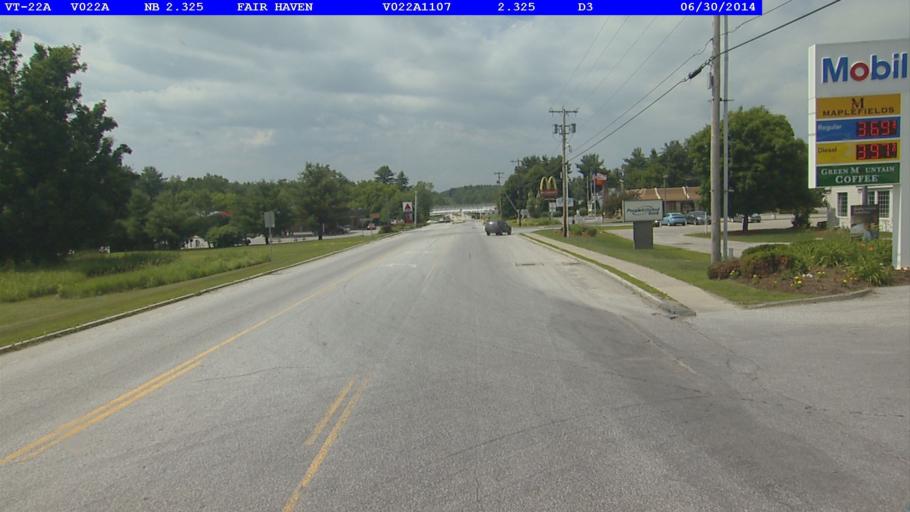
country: US
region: Vermont
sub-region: Rutland County
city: Fair Haven
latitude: 43.6032
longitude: -73.2756
